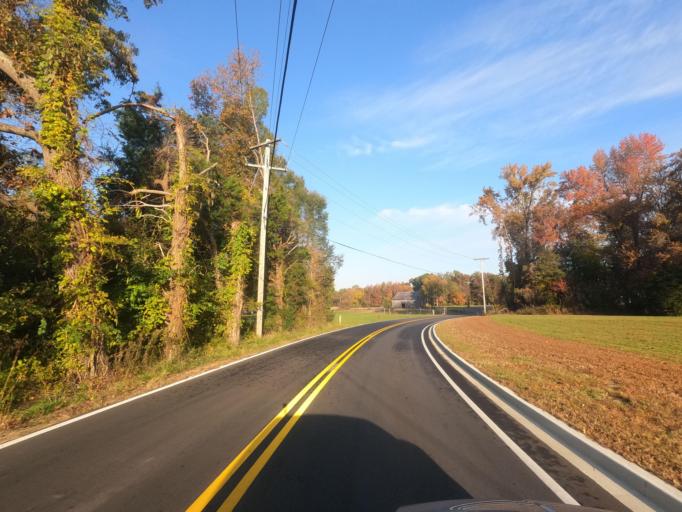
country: US
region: Maryland
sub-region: Saint Mary's County
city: Golden Beach
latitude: 38.4969
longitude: -76.6354
